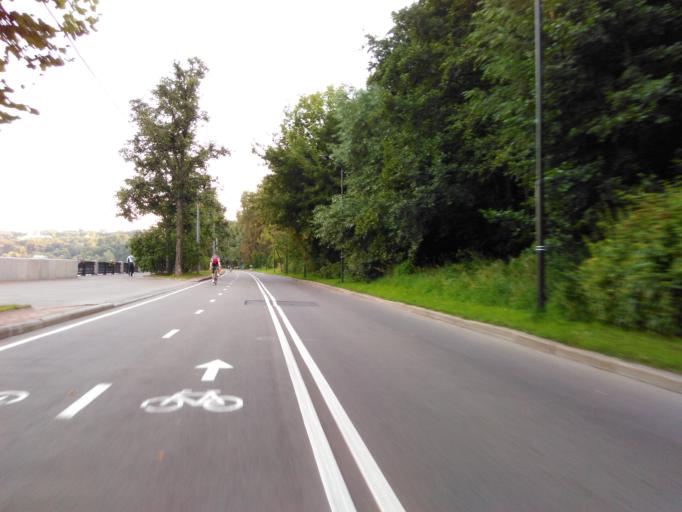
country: RU
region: Moscow
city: Vorob'yovo
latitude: 55.7224
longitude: 37.5395
